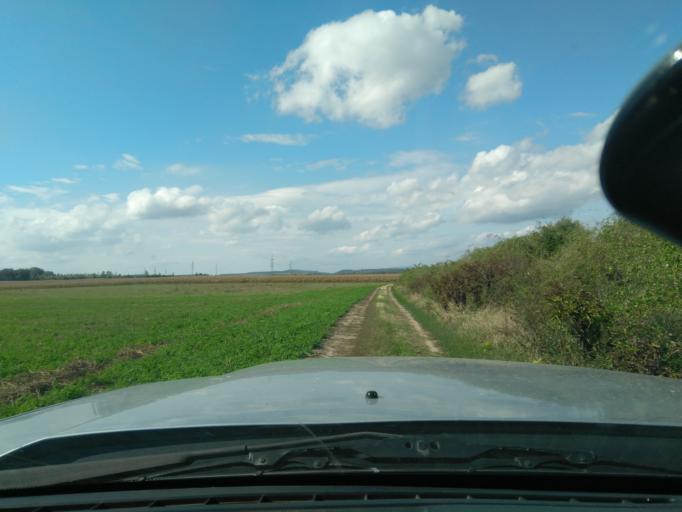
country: HU
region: Fejer
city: Bicske
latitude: 47.4735
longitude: 18.6708
